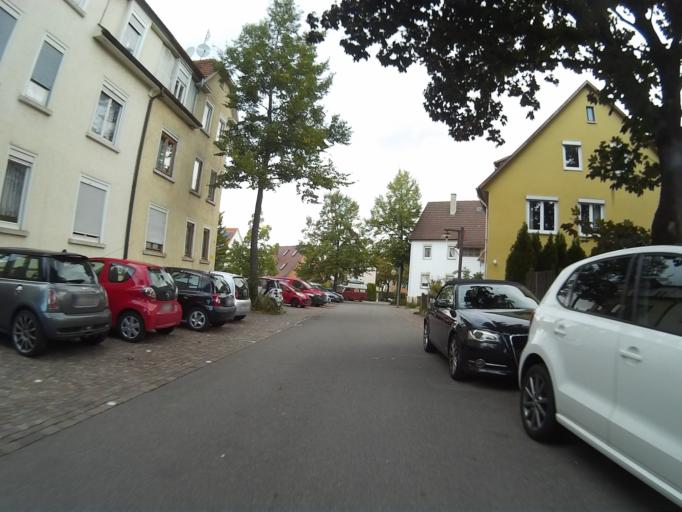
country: DE
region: Baden-Wuerttemberg
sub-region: Tuebingen Region
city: Pfullingen
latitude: 48.4673
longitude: 9.2235
